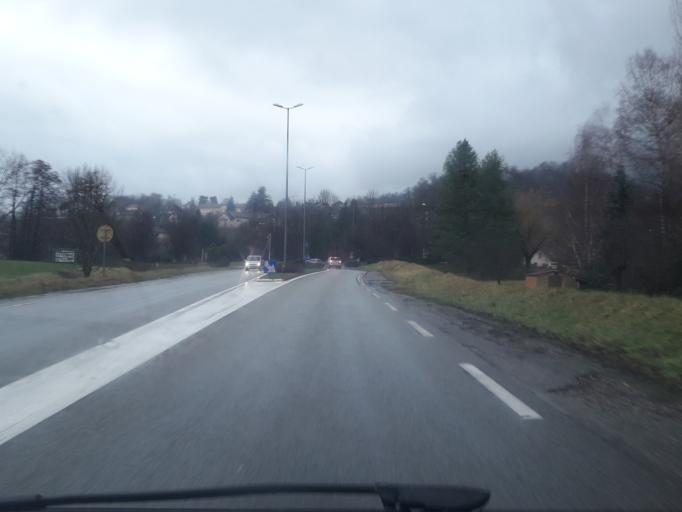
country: FR
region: Rhone-Alpes
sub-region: Departement de la Savoie
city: Le Bourget-du-Lac
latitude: 45.6443
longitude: 5.8638
